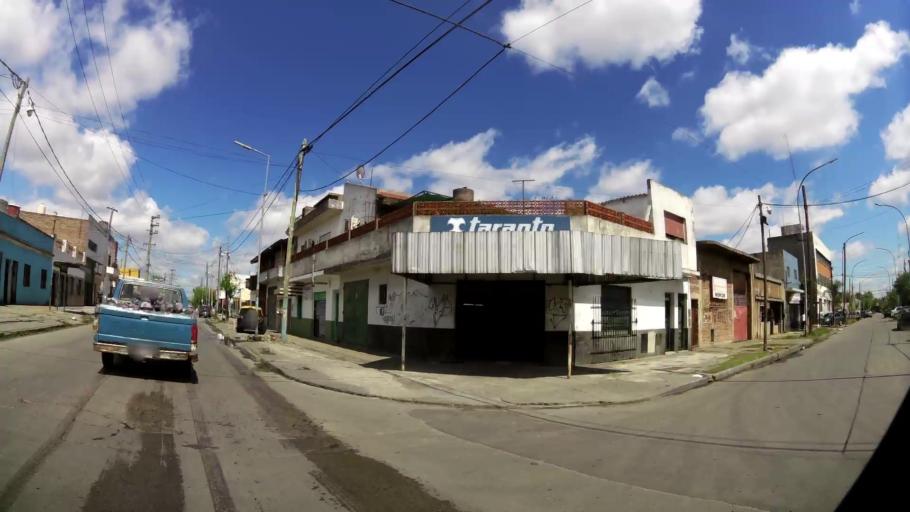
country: AR
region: Buenos Aires
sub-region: Partido de Lanus
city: Lanus
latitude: -34.6734
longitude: -58.4267
